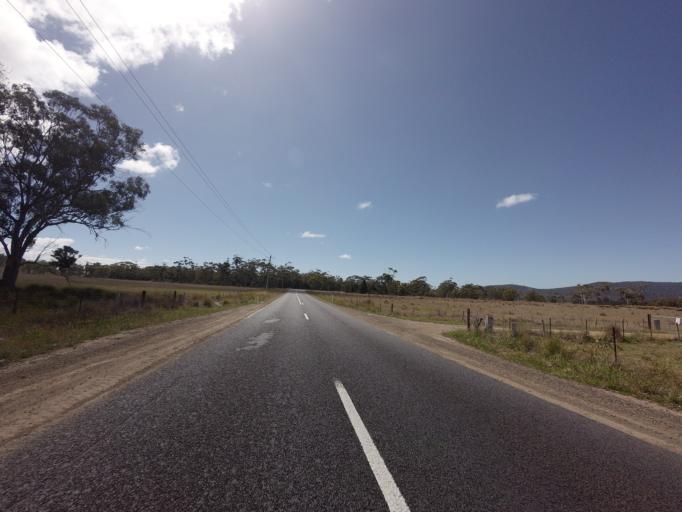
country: AU
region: Tasmania
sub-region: Break O'Day
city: St Helens
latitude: -41.9189
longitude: 148.2439
